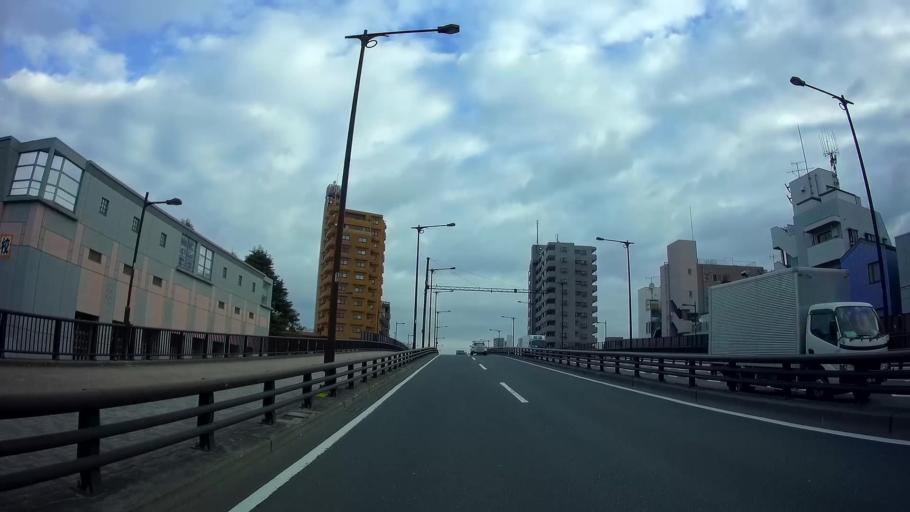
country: JP
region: Tokyo
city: Tokyo
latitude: 35.7143
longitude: 139.6865
